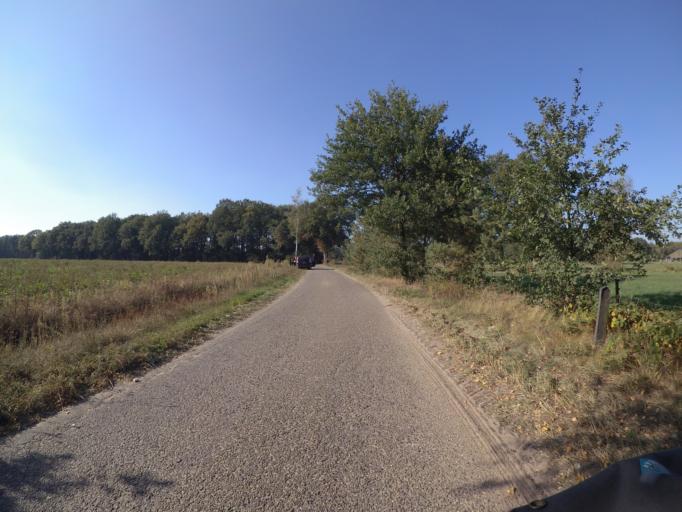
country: NL
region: North Brabant
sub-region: Gemeente Oirschot
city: Oirschot
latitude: 51.4885
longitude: 5.3233
